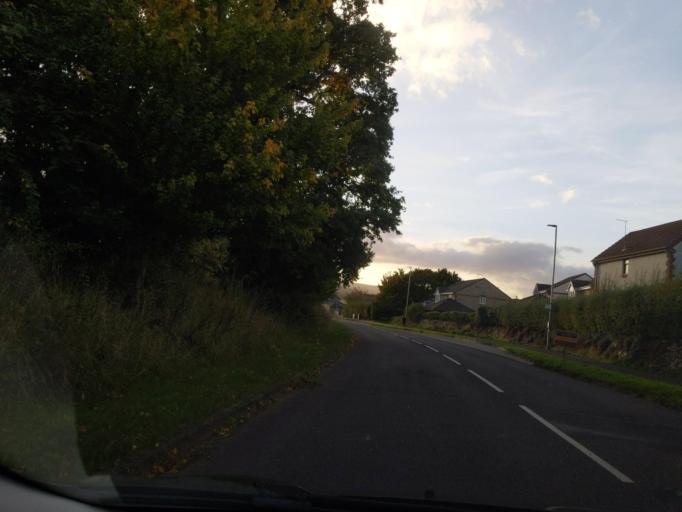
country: GB
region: England
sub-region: Devon
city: Bovey Tracey
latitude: 50.5918
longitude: -3.6700
